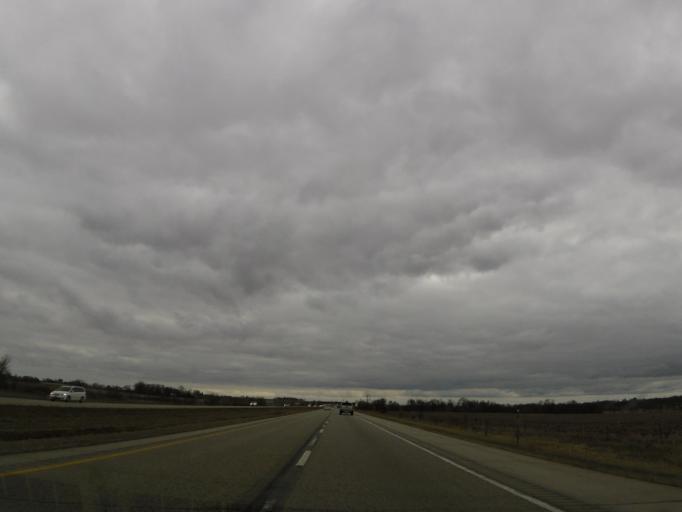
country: US
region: Iowa
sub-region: Linn County
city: Center Point
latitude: 42.1648
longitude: -91.7703
